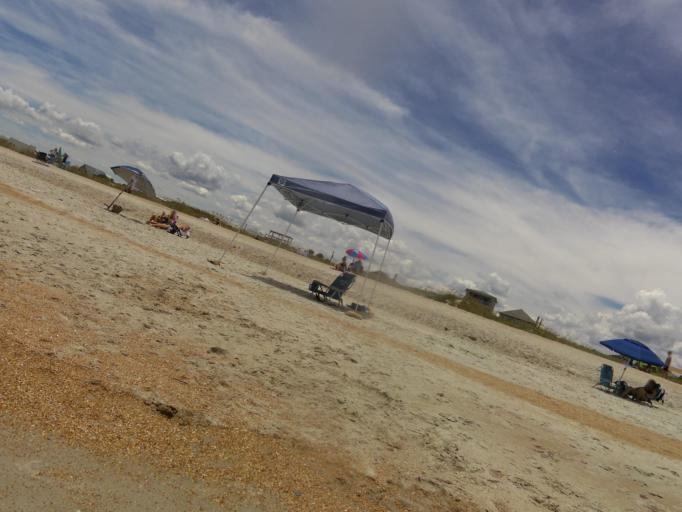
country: US
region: Florida
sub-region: Saint Johns County
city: Saint Augustine Beach
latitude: 29.8503
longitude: -81.2643
